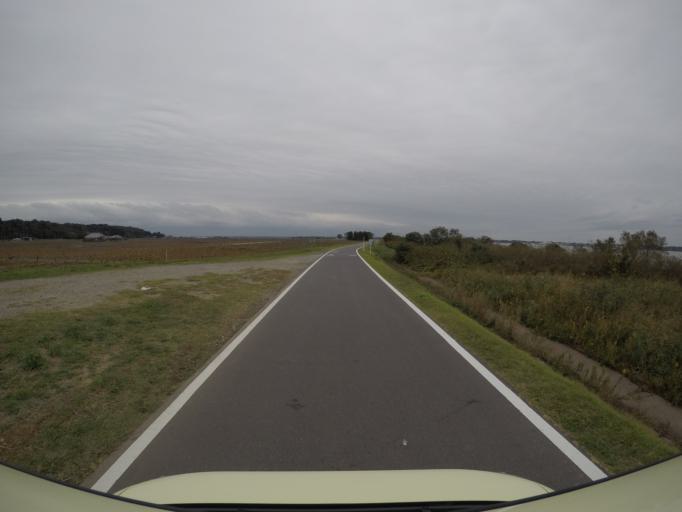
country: JP
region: Ibaraki
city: Ami
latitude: 36.0796
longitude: 140.2389
